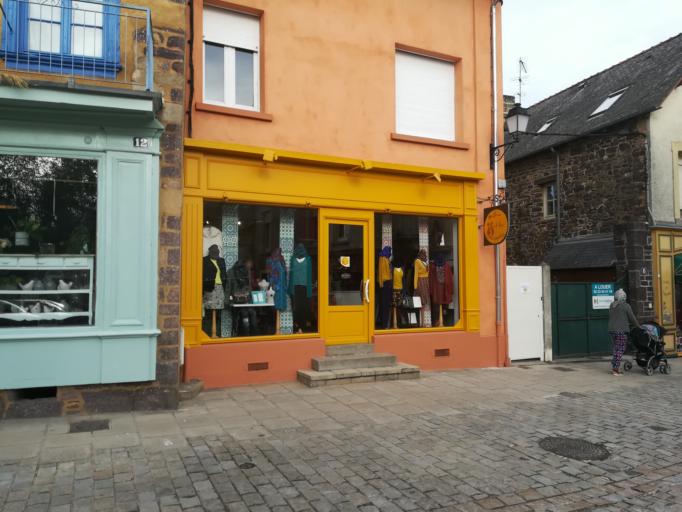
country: FR
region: Brittany
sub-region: Departement d'Ille-et-Vilaine
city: Montfort-sur-Meu
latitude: 48.1369
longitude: -1.9547
